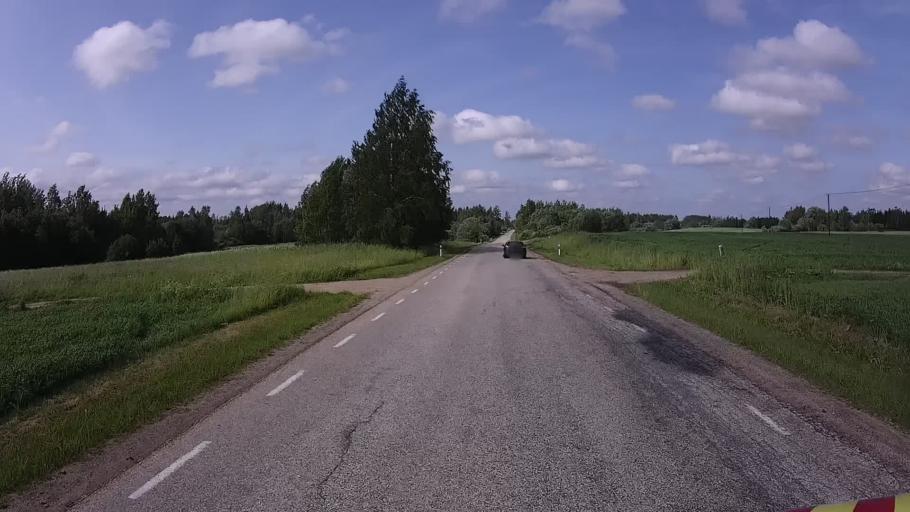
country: EE
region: Vorumaa
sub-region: Antsla vald
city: Vana-Antsla
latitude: 57.8513
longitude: 26.5834
